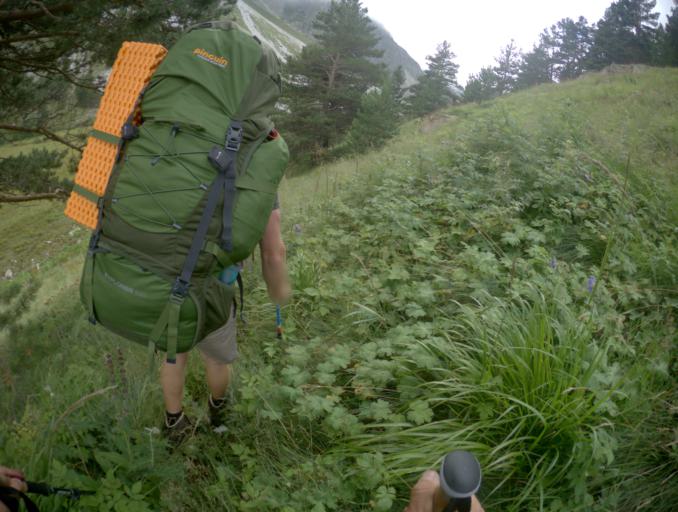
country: RU
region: Karachayevo-Cherkesiya
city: Uchkulan
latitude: 43.3370
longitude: 42.1274
